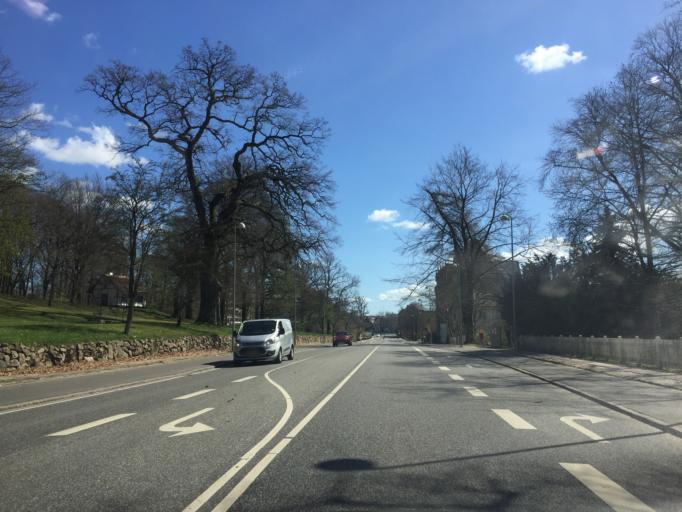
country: DK
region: Capital Region
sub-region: Lyngby-Tarbaek Kommune
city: Kongens Lyngby
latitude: 55.7764
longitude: 12.4963
